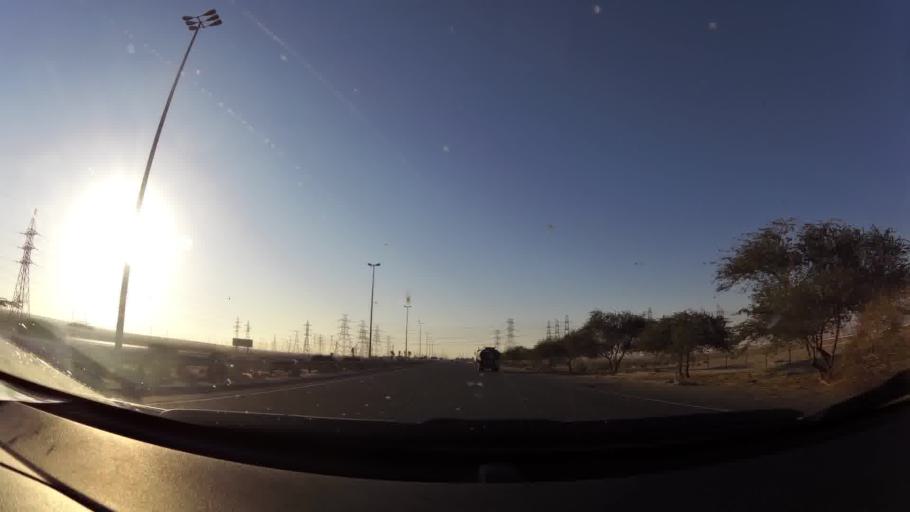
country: KW
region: Al Ahmadi
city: Al Fahahil
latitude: 28.7626
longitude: 48.2791
